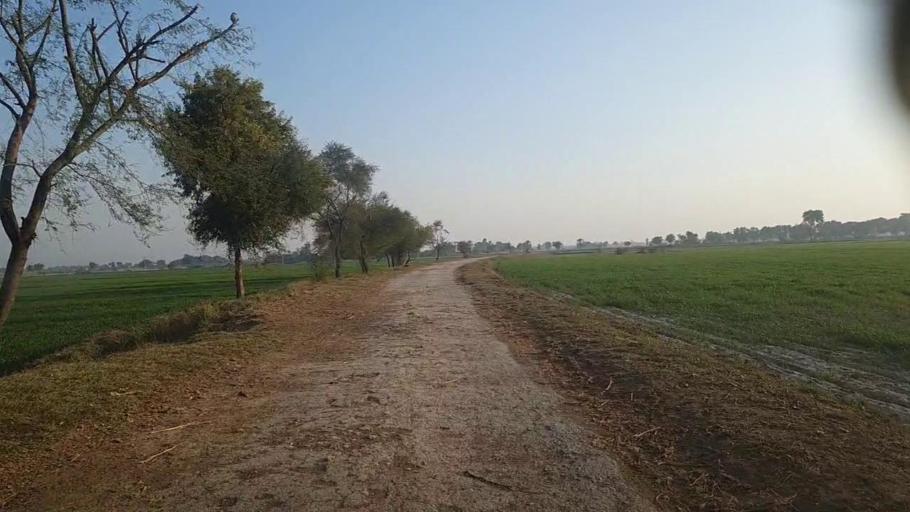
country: PK
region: Sindh
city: Khairpur
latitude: 28.0728
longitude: 69.7494
